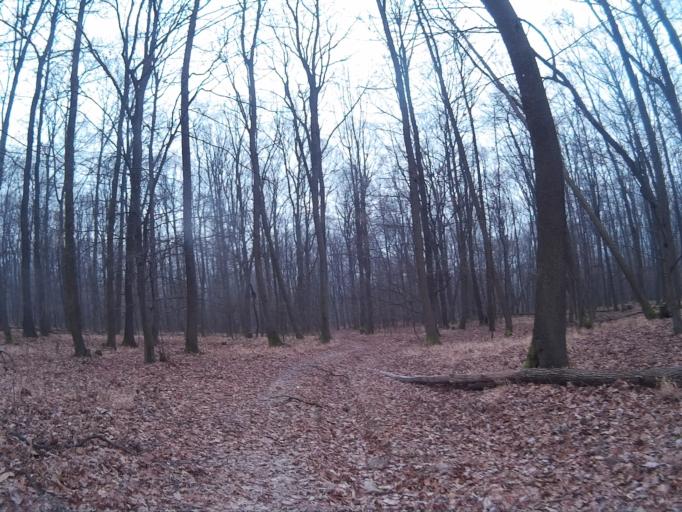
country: HU
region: Nograd
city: Rimoc
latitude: 47.9789
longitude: 19.5692
